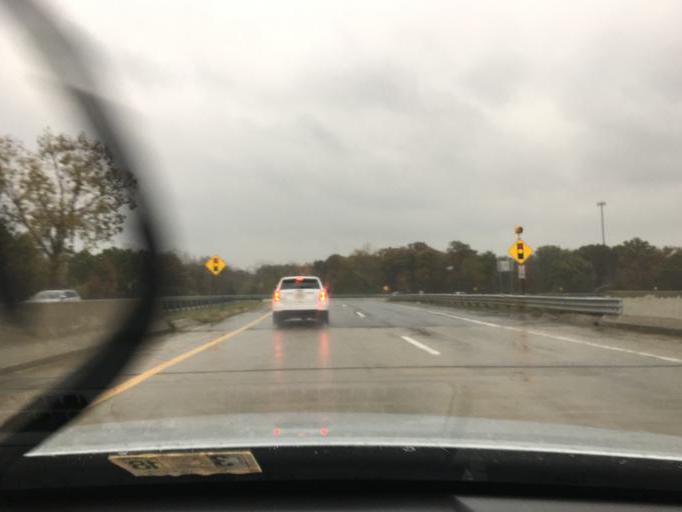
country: US
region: Michigan
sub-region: Oakland County
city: Auburn Hills
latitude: 42.6931
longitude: -83.2420
